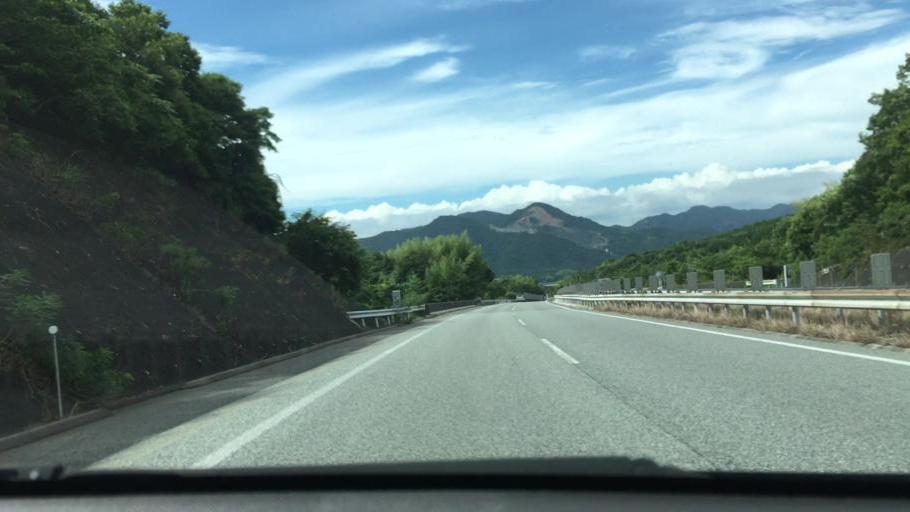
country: JP
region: Yamaguchi
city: Hofu
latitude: 34.0590
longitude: 131.5033
